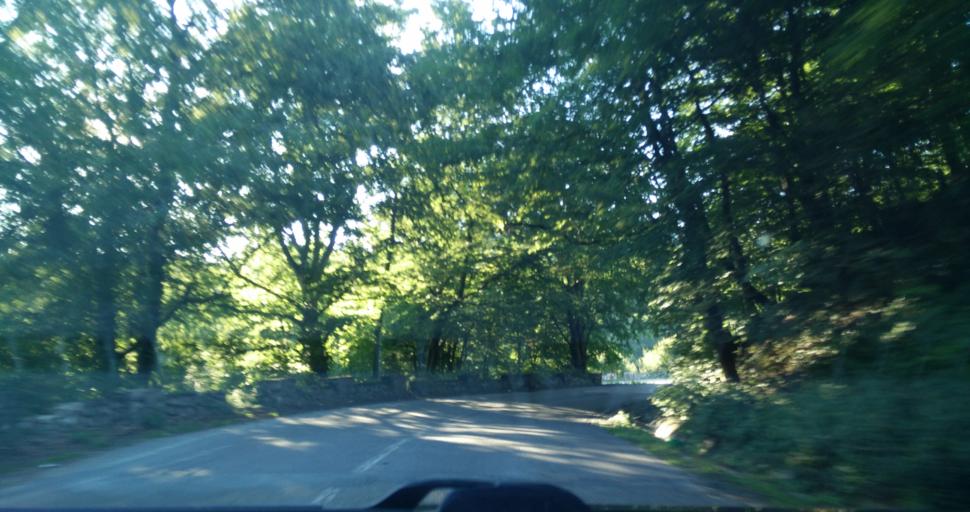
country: RO
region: Bihor
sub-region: Oras Nucet
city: Nucet
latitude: 46.4876
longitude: 22.6054
